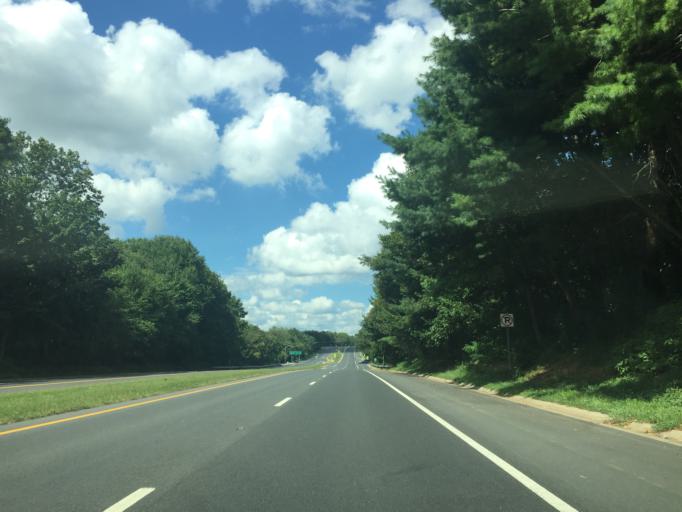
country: US
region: Maryland
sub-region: Montgomery County
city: Redland
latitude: 39.1425
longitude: -77.1565
